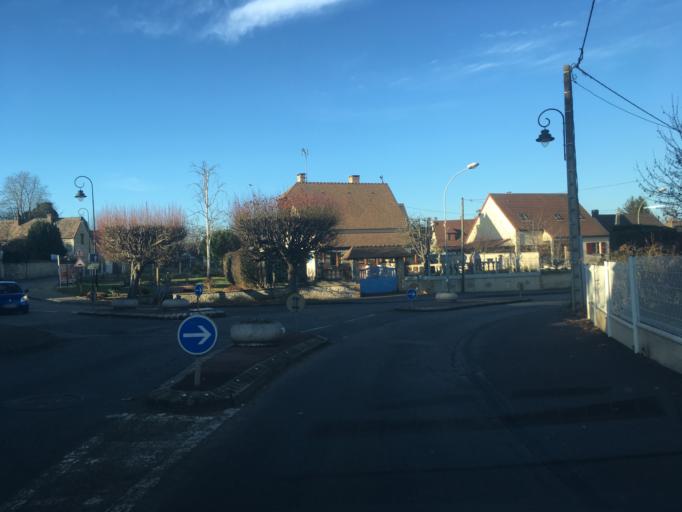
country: FR
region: Haute-Normandie
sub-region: Departement de l'Eure
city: Saint-Marcel
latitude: 49.0987
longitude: 1.4468
